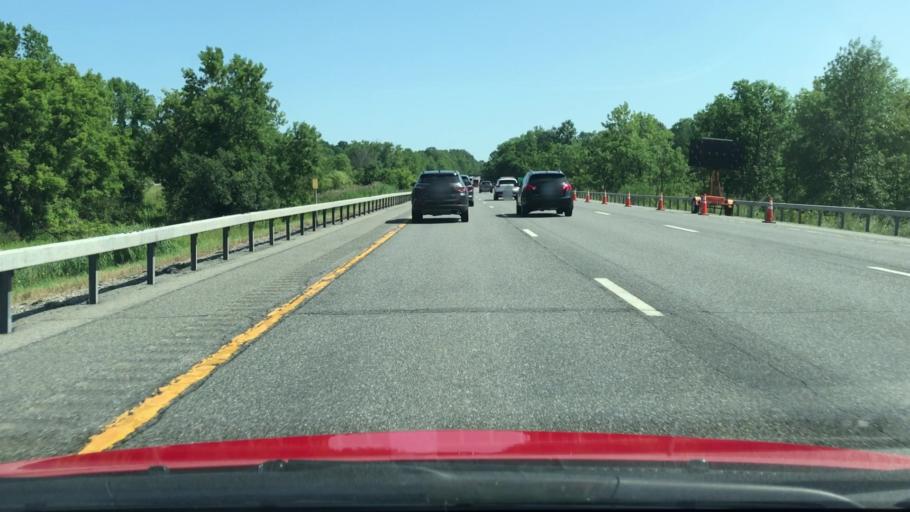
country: US
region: New York
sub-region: Saratoga County
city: Saratoga Springs
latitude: 43.0399
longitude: -73.7762
